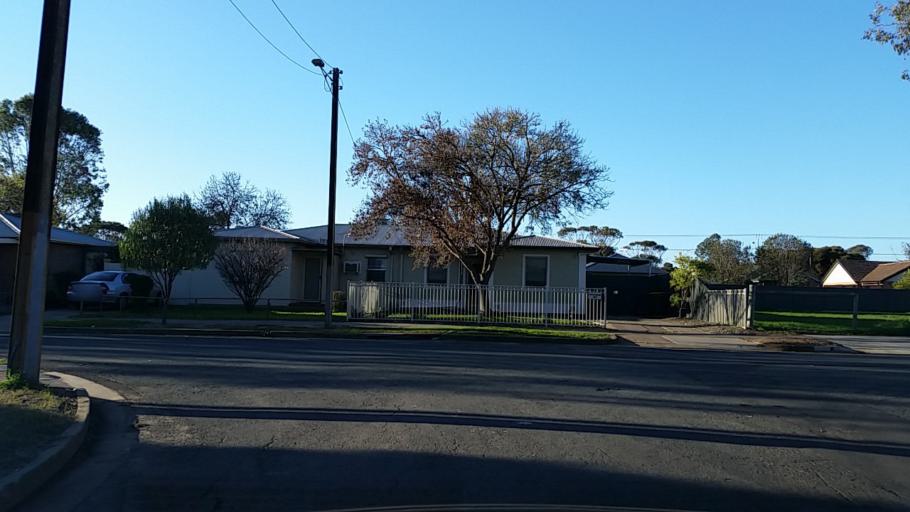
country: AU
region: South Australia
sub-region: Playford
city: Smithfield
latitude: -34.6805
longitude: 138.6690
